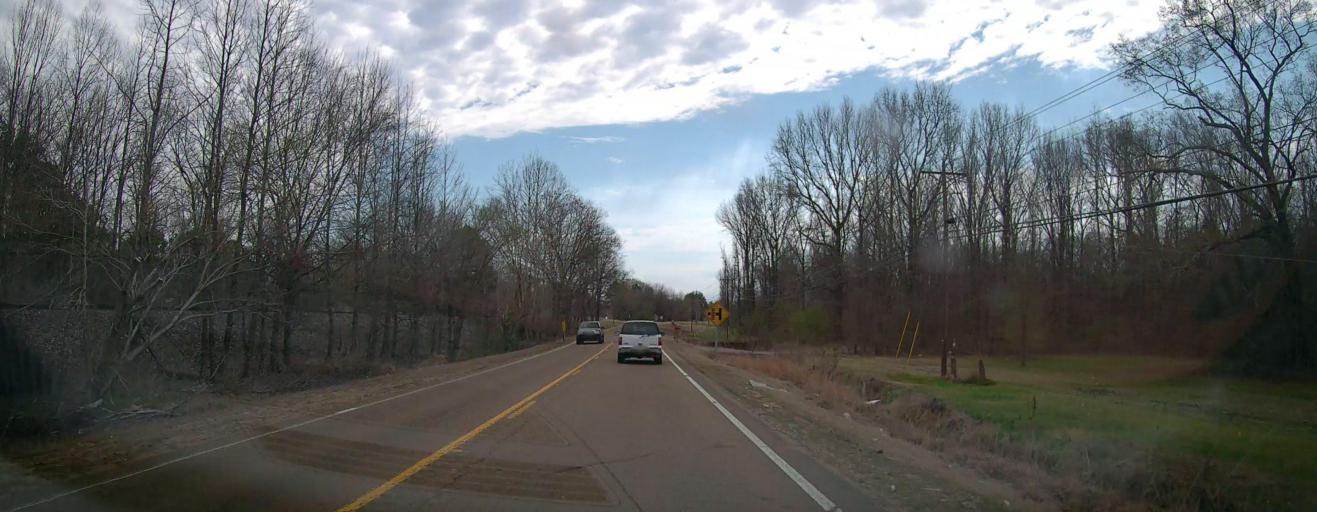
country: US
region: Mississippi
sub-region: Marshall County
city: Byhalia
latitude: 34.8801
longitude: -89.7097
